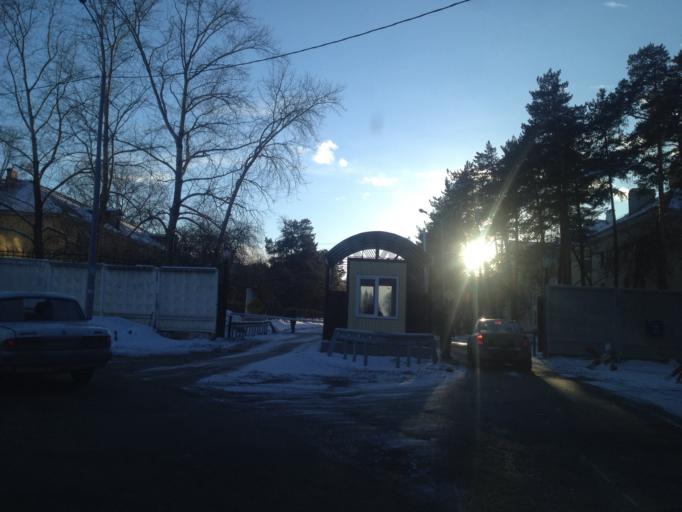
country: RU
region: Sverdlovsk
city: Sovkhoznyy
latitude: 56.7808
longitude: 60.5962
